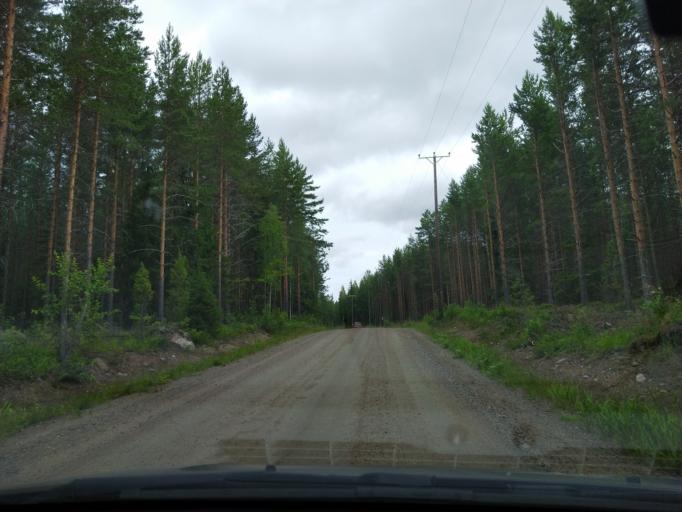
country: FI
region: Southern Savonia
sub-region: Mikkeli
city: Maentyharju
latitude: 61.1421
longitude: 26.8907
